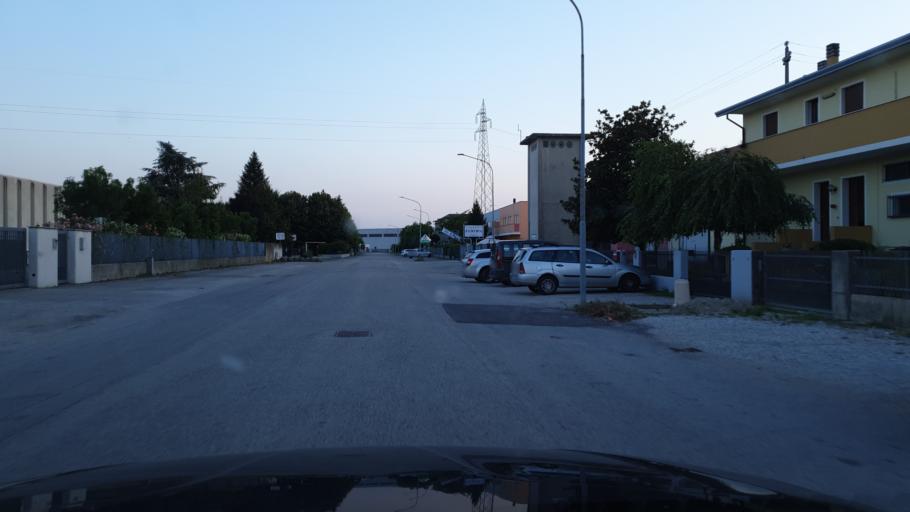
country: IT
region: Veneto
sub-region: Provincia di Rovigo
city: Grignano Polesine
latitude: 45.0323
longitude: 11.7735
